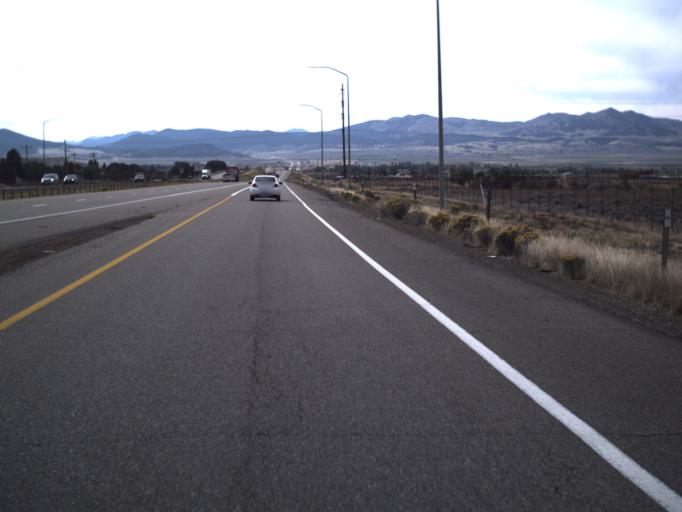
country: US
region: Utah
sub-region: Beaver County
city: Beaver
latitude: 38.2889
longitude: -112.6509
